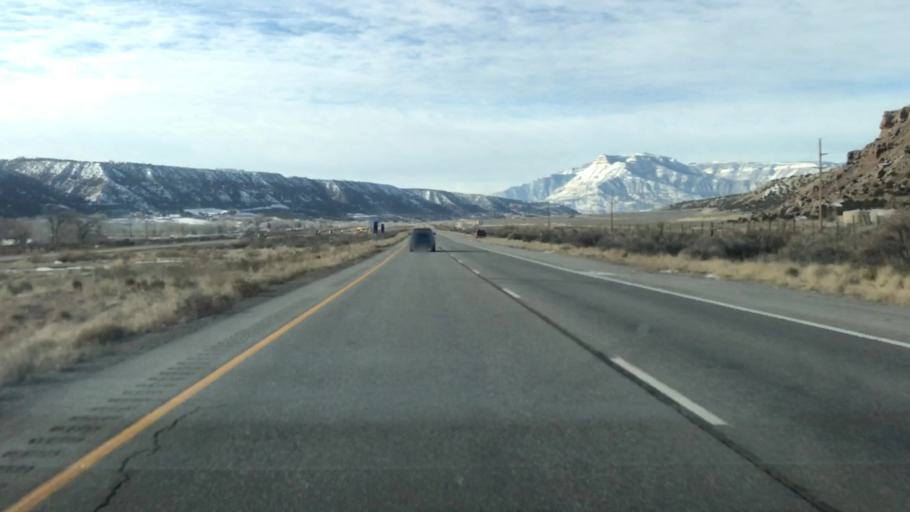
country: US
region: Colorado
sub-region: Garfield County
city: Battlement Mesa
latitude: 39.4879
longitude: -107.9581
